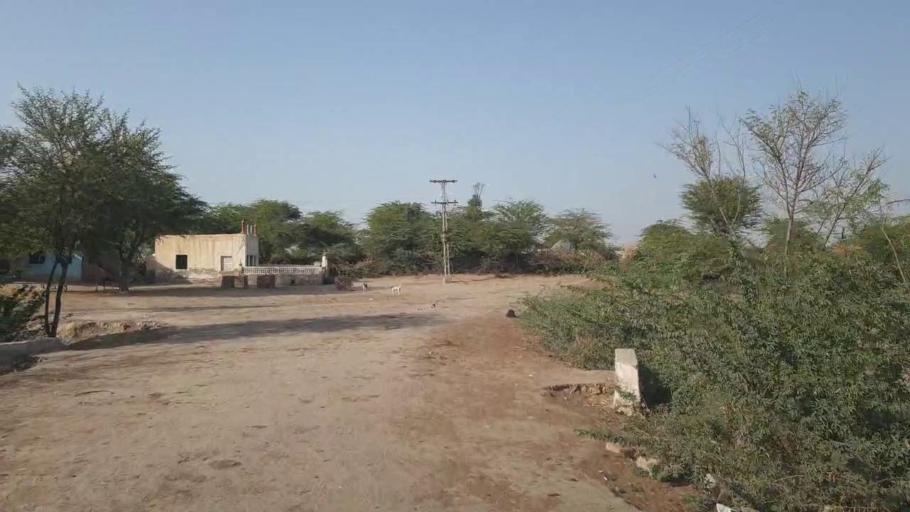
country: PK
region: Sindh
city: Dhoro Naro
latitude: 25.4690
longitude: 69.5548
